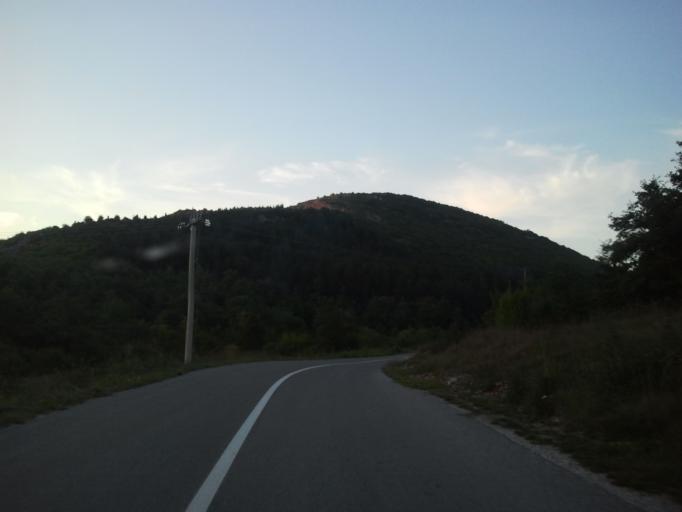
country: HR
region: Zadarska
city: Obrovac
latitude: 44.4270
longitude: 15.6600
